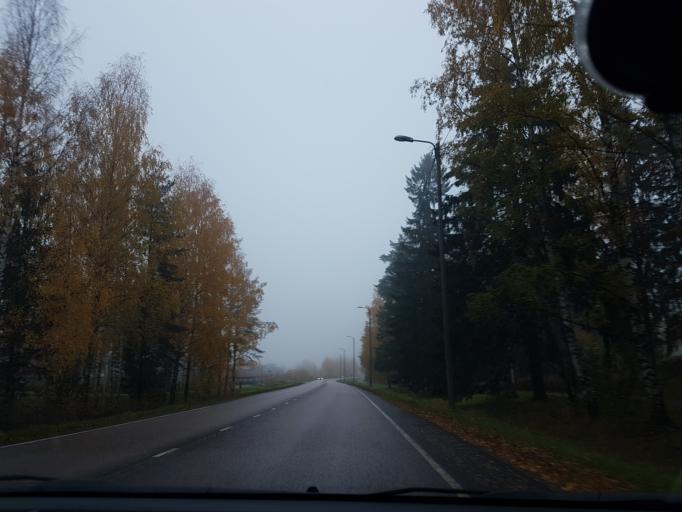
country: FI
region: Uusimaa
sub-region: Helsinki
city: Tuusula
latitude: 60.4054
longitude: 25.0360
